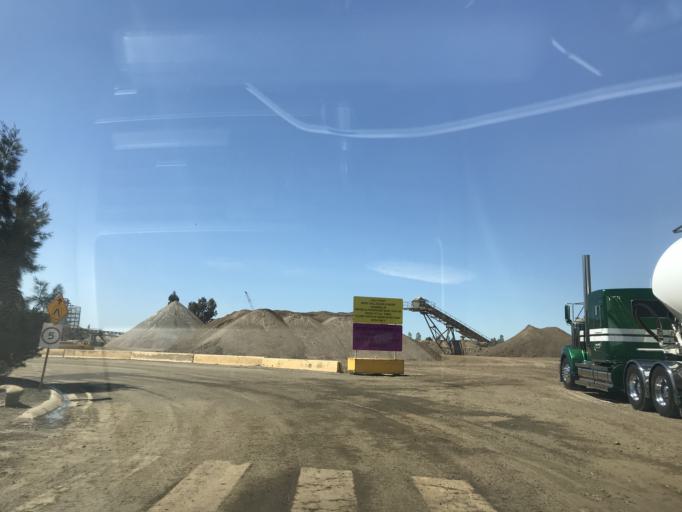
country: AU
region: Victoria
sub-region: Hobsons Bay
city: Laverton
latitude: -37.8339
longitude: 144.7729
